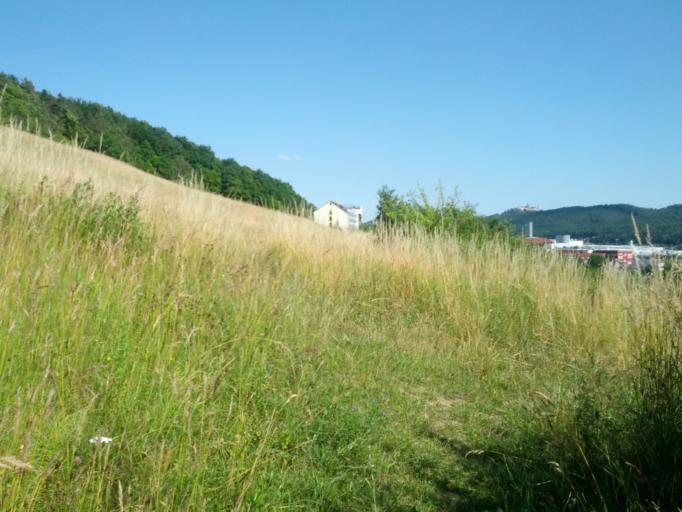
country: DE
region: Thuringia
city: Krauthausen
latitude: 50.9913
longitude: 10.2646
